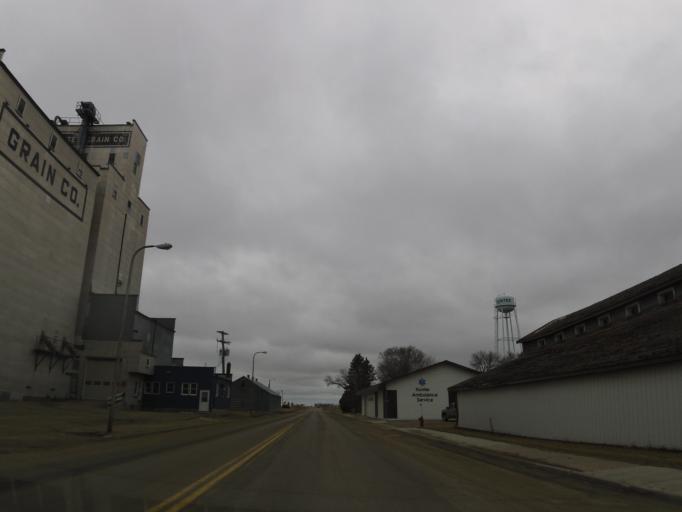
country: US
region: North Dakota
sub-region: Traill County
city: Hillsboro
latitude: 47.1911
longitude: -97.2174
